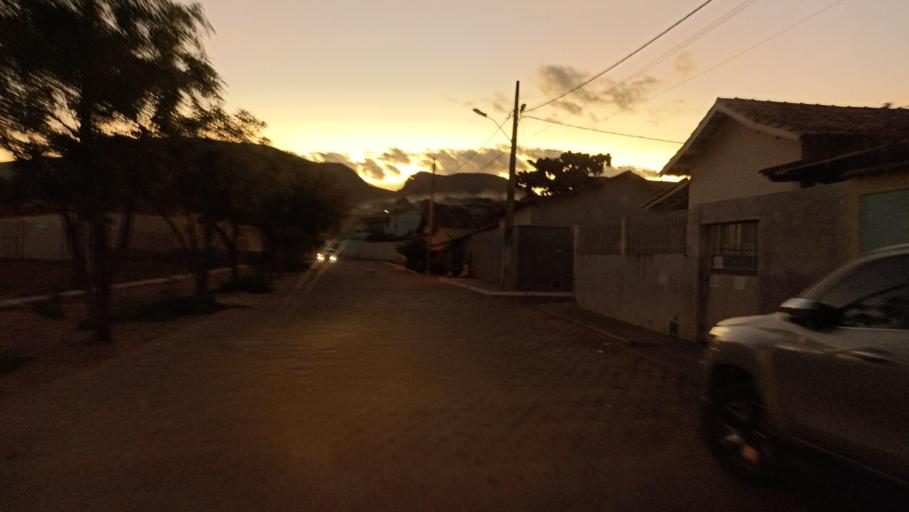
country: BR
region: Minas Gerais
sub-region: Aracuai
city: Aracuai
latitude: -16.6185
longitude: -42.1840
